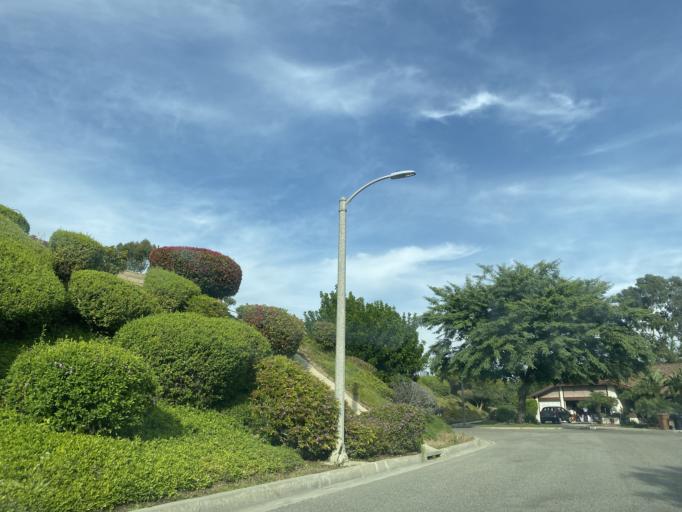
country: US
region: California
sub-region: Orange County
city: Brea
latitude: 33.8950
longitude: -117.8881
